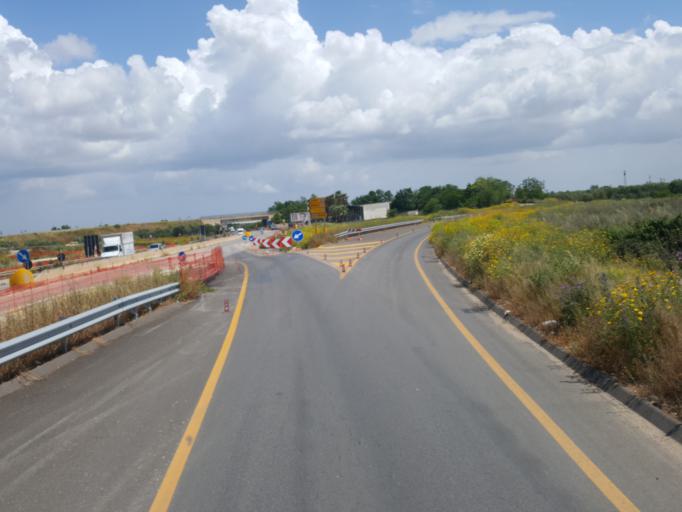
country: IT
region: Apulia
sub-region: Provincia di Bari
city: Bitetto
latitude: 41.0732
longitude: 16.7493
